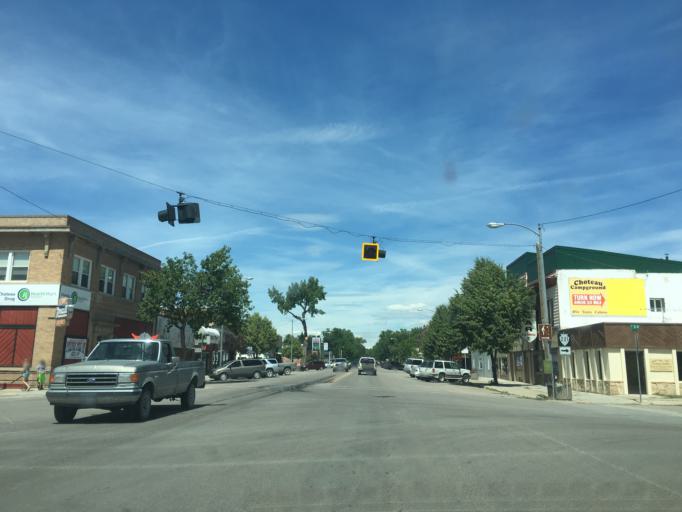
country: US
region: Montana
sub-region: Teton County
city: Choteau
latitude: 47.8121
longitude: -112.1834
